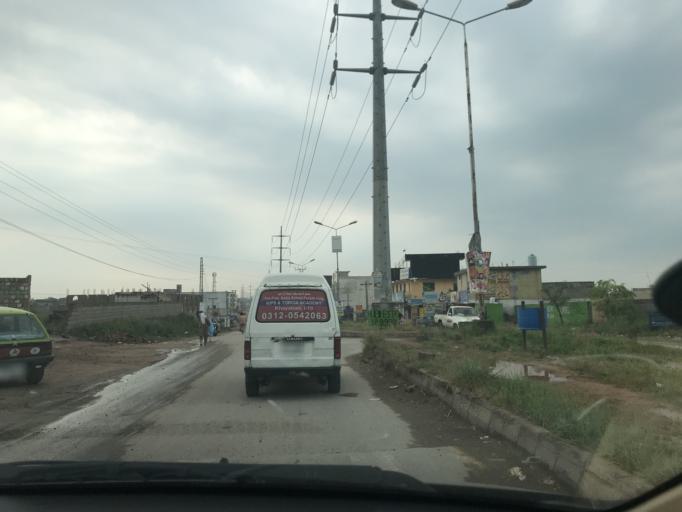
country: PK
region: Islamabad
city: Islamabad
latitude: 33.6848
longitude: 73.1612
